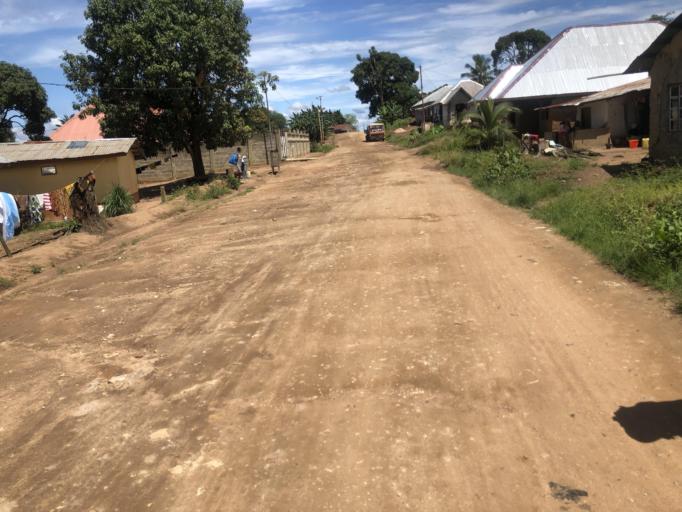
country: SL
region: Eastern Province
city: Koidu
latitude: 8.6417
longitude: -10.9573
